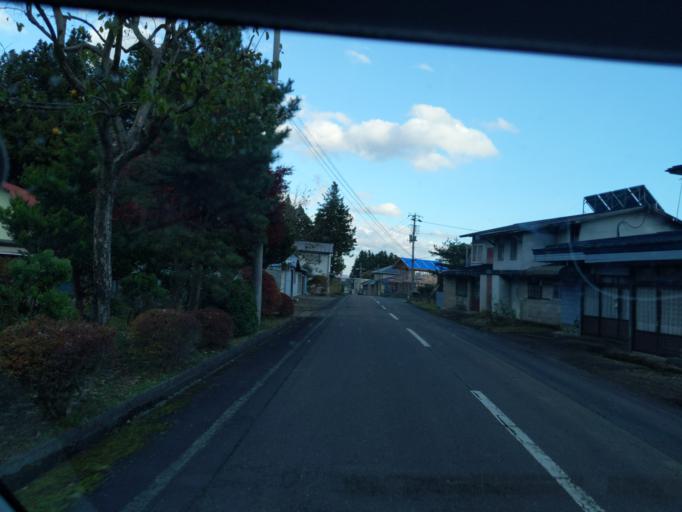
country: JP
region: Iwate
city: Mizusawa
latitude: 39.0771
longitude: 141.0461
